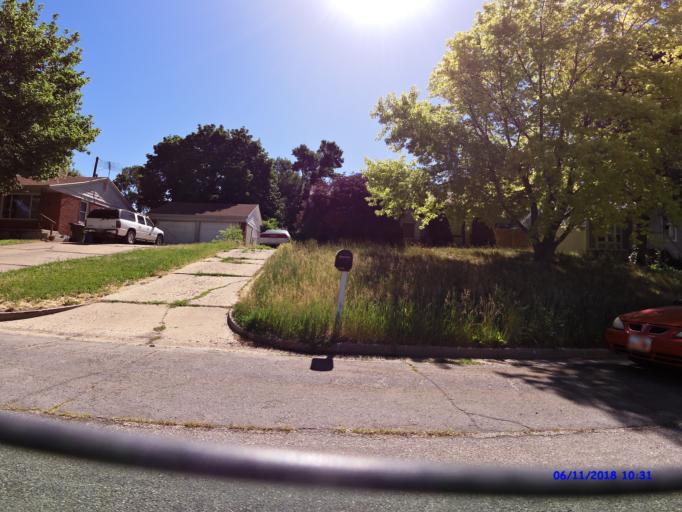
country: US
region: Utah
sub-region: Weber County
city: Ogden
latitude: 41.2283
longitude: -111.9410
